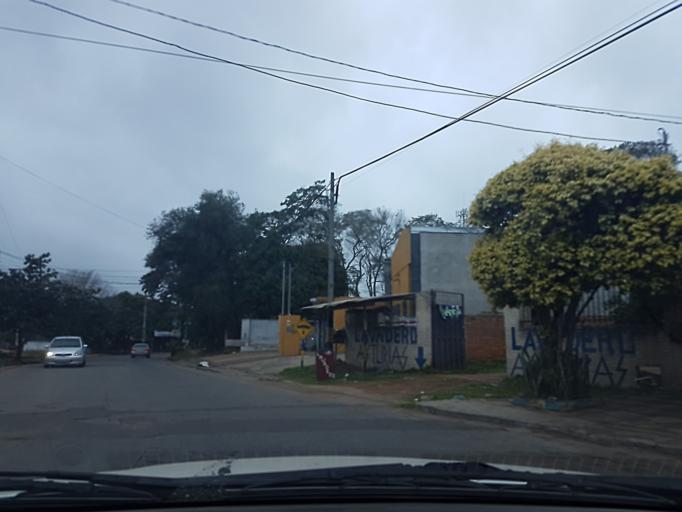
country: PY
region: Central
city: San Lorenzo
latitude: -25.2706
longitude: -57.4789
